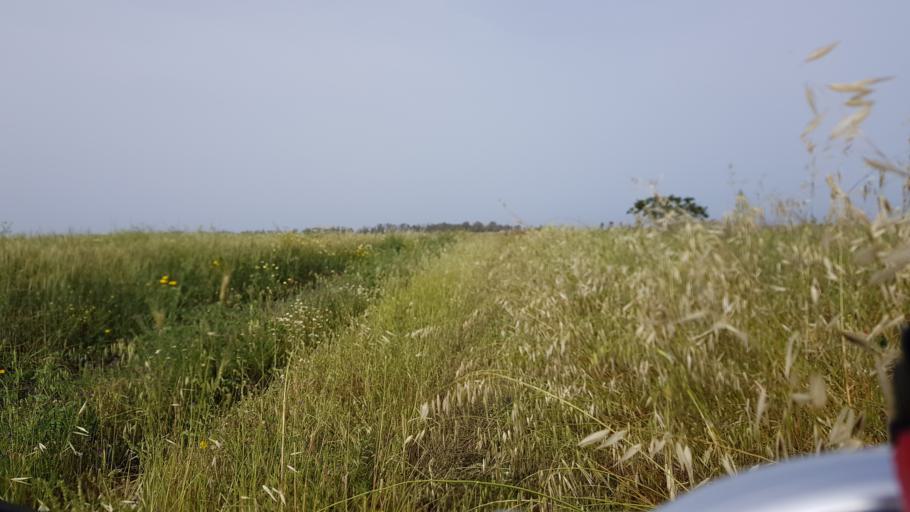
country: IT
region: Apulia
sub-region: Provincia di Brindisi
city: La Rosa
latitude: 40.5770
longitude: 18.0261
